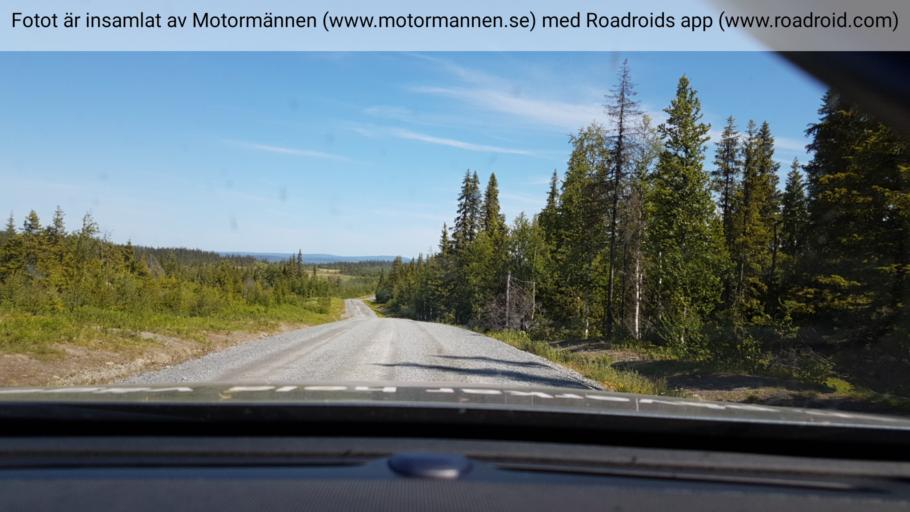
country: SE
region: Vaesterbotten
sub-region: Vilhelmina Kommun
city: Sjoberg
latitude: 64.7668
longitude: 15.9004
